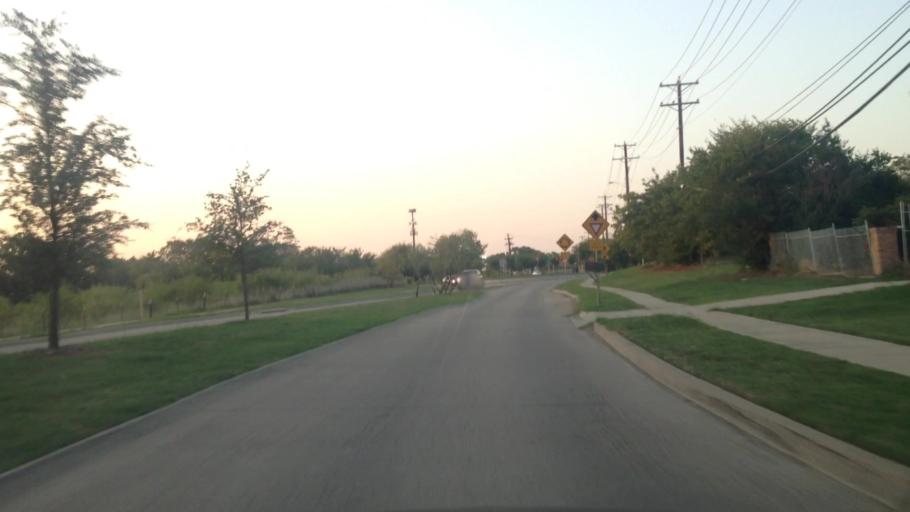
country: US
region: Texas
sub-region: Tarrant County
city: Kennedale
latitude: 32.6457
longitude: -97.2086
